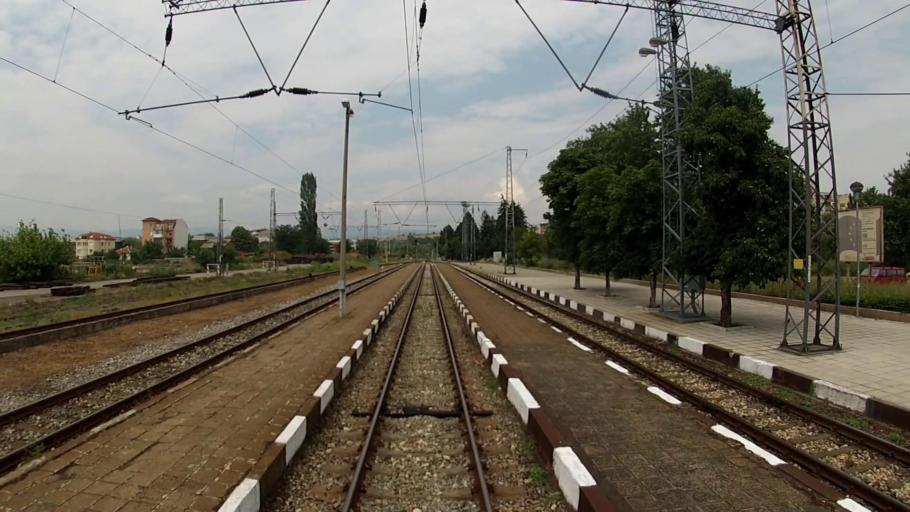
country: BG
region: Blagoevgrad
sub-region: Obshtina Blagoevgrad
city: Blagoevgrad
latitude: 42.0092
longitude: 23.0914
